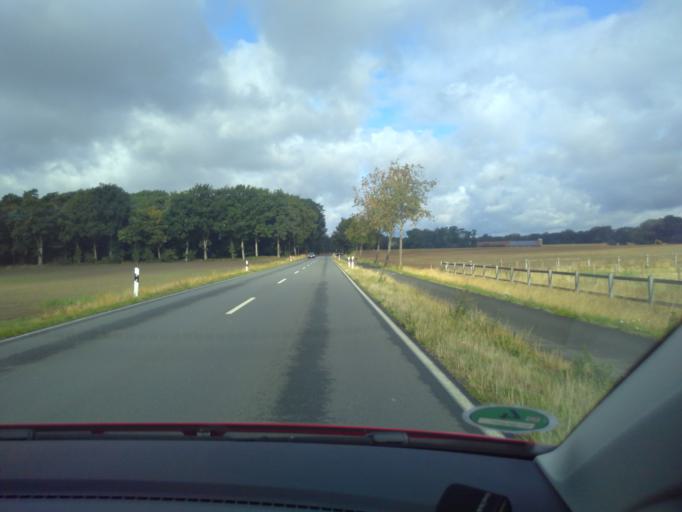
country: DE
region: North Rhine-Westphalia
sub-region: Regierungsbezirk Munster
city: Warendorf
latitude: 51.9687
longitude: 7.9696
